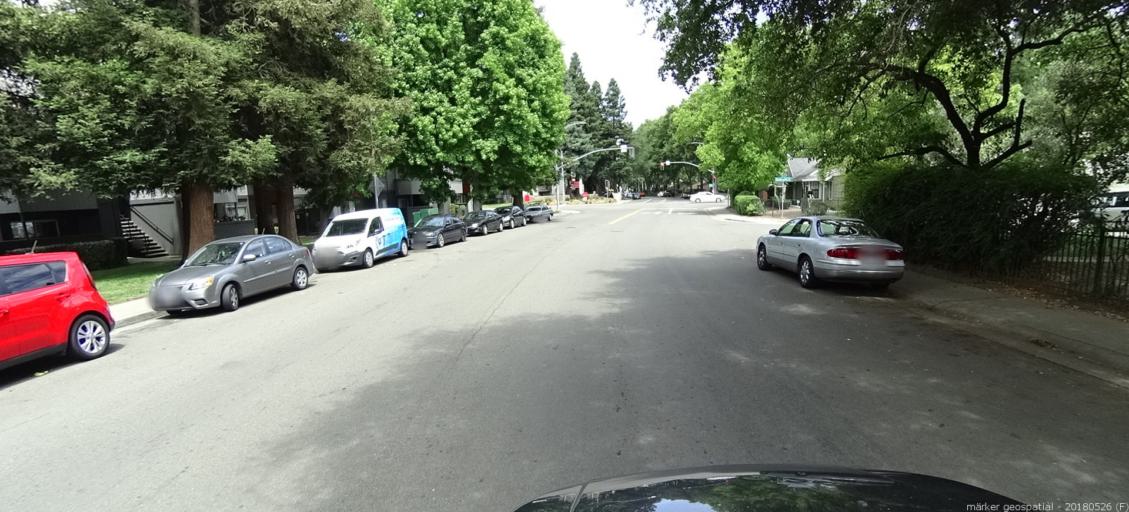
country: US
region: California
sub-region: Sacramento County
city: Sacramento
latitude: 38.6122
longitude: -121.4932
